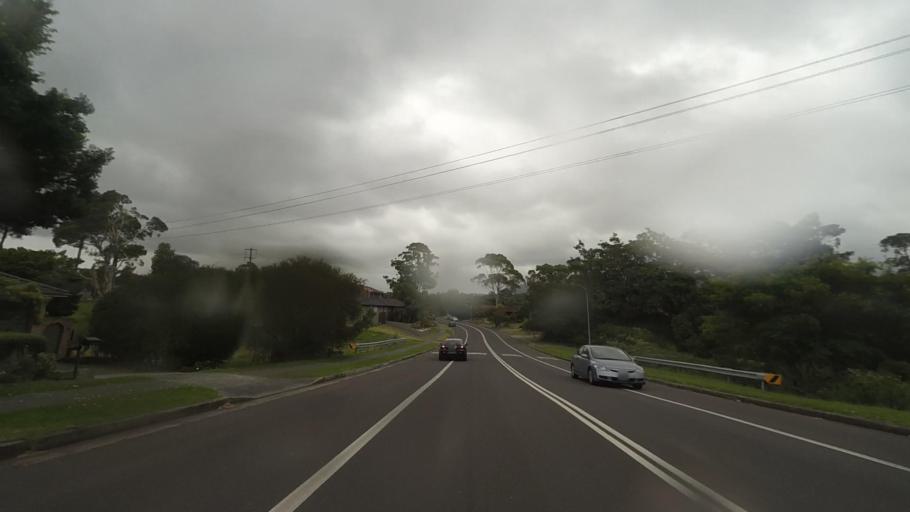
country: AU
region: New South Wales
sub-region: Wollongong
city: Cordeaux Heights
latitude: -34.4421
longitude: 150.8465
